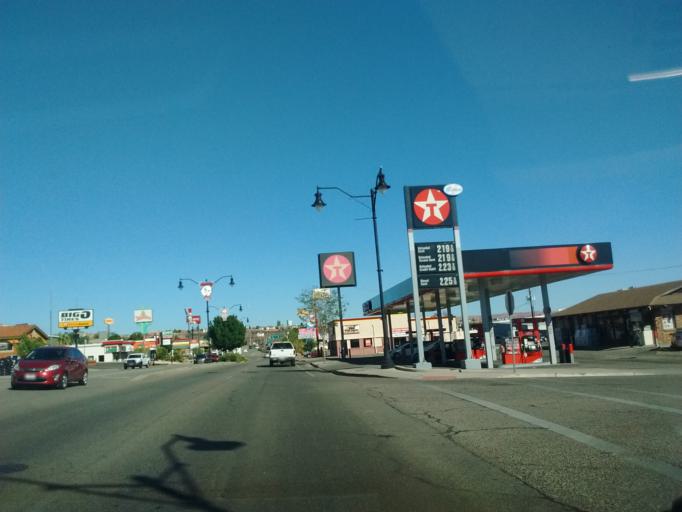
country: US
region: Utah
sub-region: Washington County
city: Saint George
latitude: 37.1097
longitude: -113.5665
